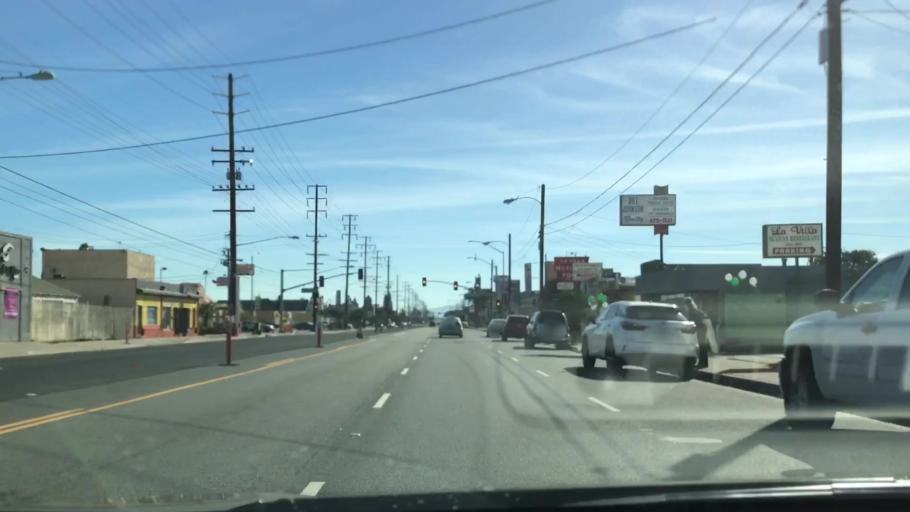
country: US
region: California
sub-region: Los Angeles County
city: Alondra Park
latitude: 33.8920
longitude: -118.3266
